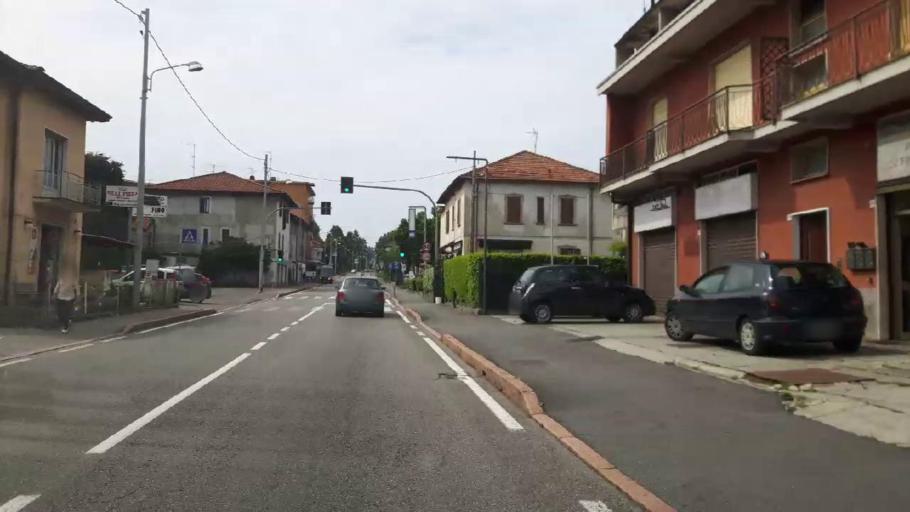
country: IT
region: Lombardy
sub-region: Provincia di Como
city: Fino Mornasco
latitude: 45.7514
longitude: 9.0504
